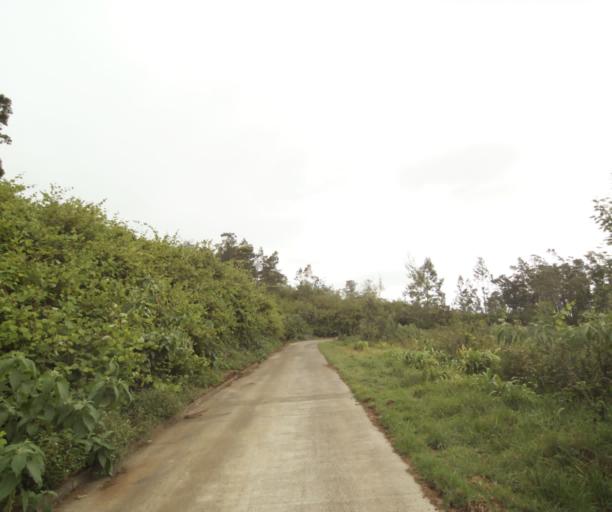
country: RE
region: Reunion
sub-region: Reunion
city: Saint-Paul
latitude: -21.0114
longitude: 55.3550
